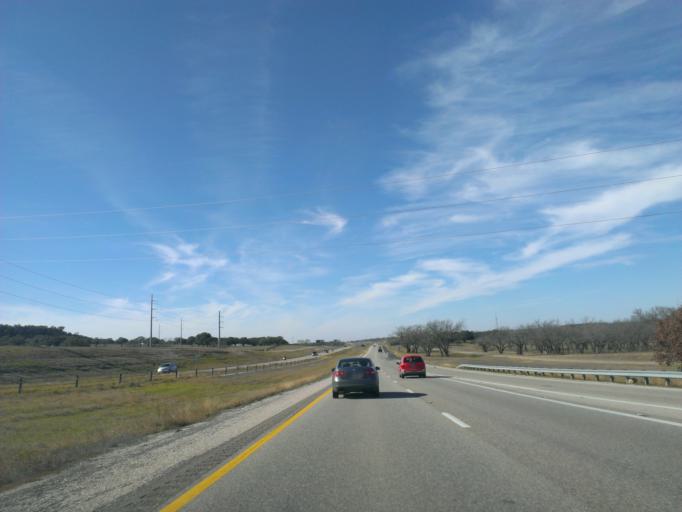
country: US
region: Texas
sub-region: Bell County
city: Nolanville
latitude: 31.0616
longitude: -97.5661
